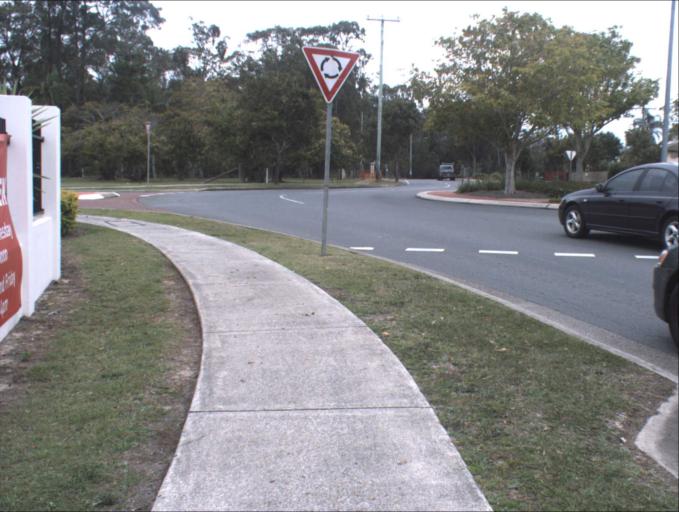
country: AU
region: Queensland
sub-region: Logan
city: Park Ridge South
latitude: -27.6861
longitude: 153.0124
